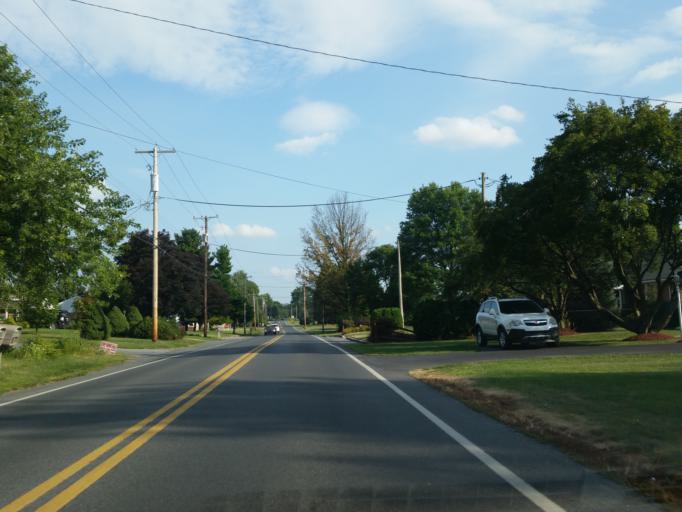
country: US
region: Pennsylvania
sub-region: Lebanon County
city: Palmyra
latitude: 40.3019
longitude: -76.5797
